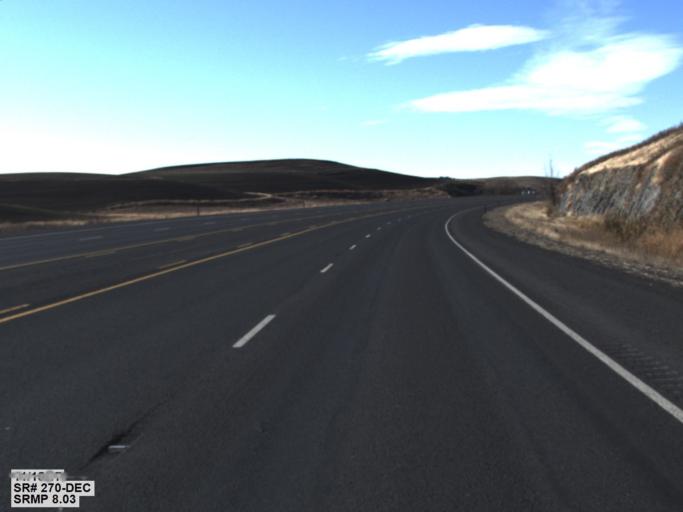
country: US
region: Idaho
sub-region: Latah County
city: Moscow
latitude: 46.7353
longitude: -117.0747
